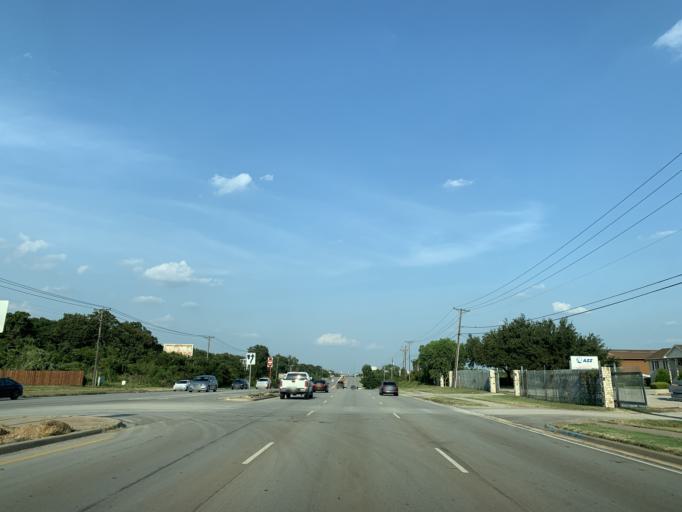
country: US
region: Texas
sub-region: Tarrant County
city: Hurst
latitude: 32.8090
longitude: -97.1828
